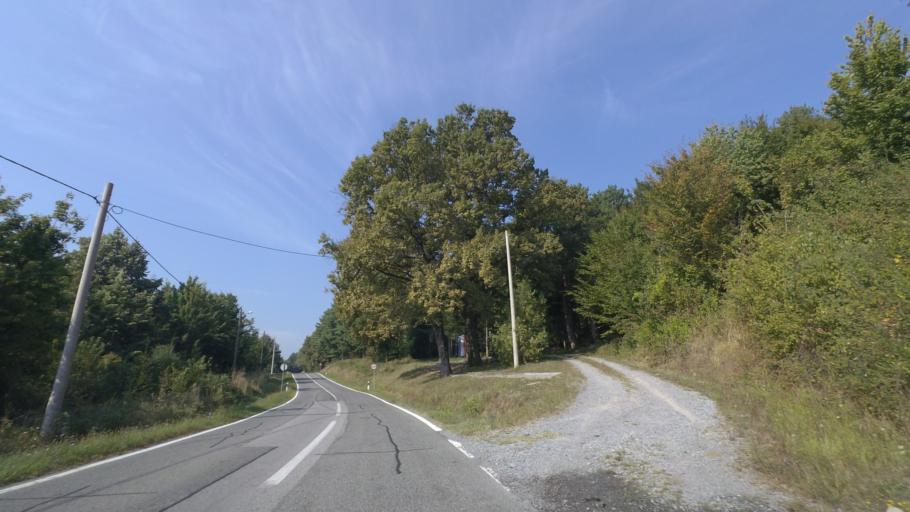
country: HR
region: Pozesko-Slavonska
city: Lipik
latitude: 45.4120
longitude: 17.0735
